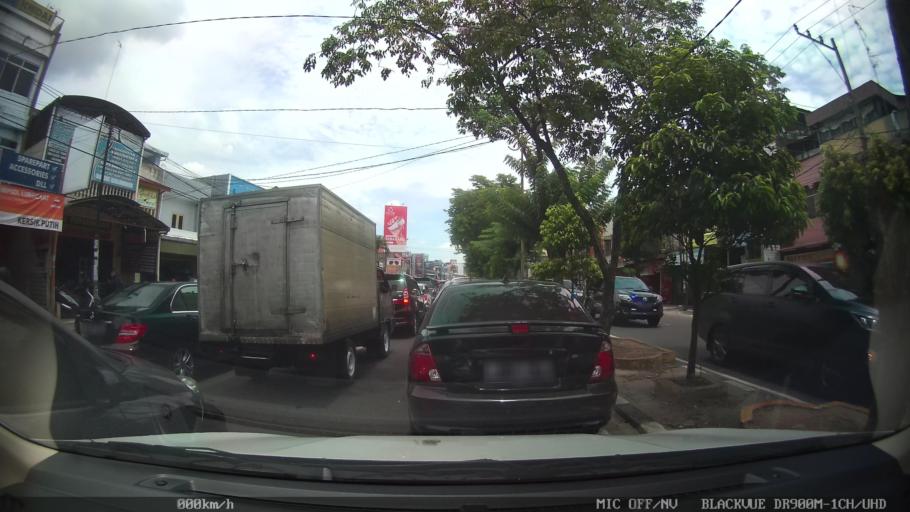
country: ID
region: North Sumatra
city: Medan
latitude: 3.5665
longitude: 98.6615
